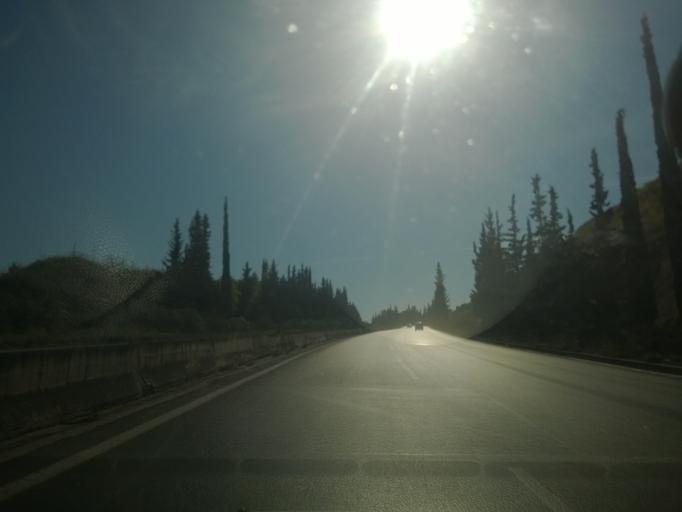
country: GR
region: Central Macedonia
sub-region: Nomos Thessalonikis
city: Neo Rysi
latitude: 40.4863
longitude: 22.9964
